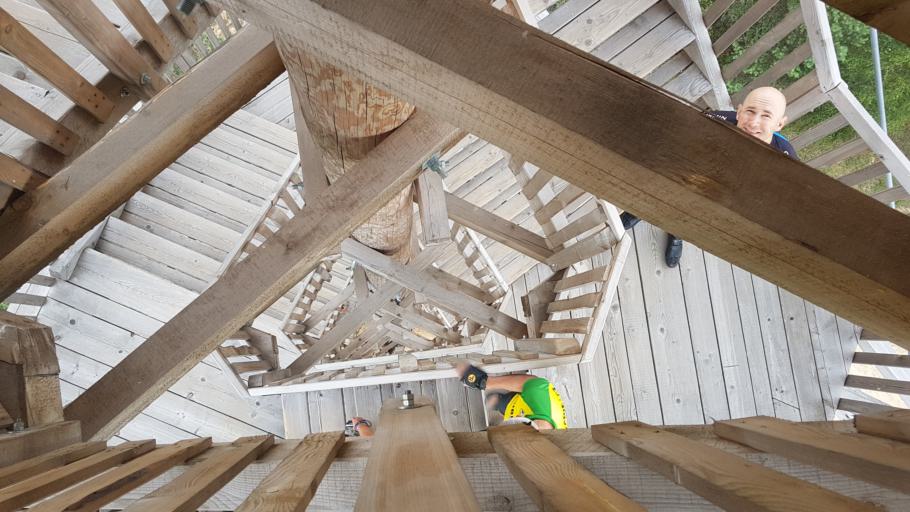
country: PL
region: Lubusz
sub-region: Powiat nowosolski
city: Kolsko
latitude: 52.0222
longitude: 16.0322
